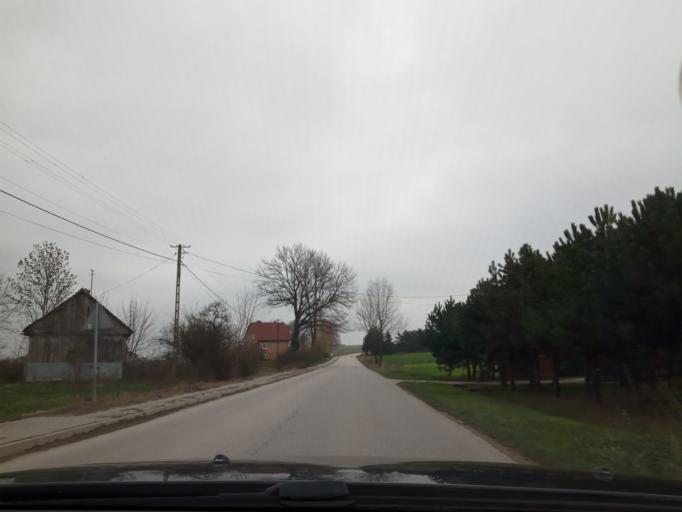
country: PL
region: Swietokrzyskie
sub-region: Powiat jedrzejowski
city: Imielno
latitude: 50.6093
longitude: 20.3926
